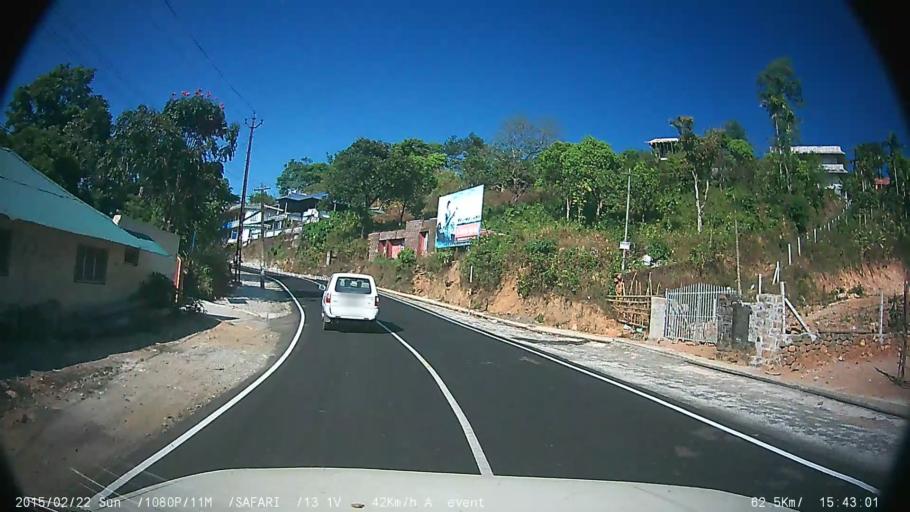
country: IN
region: Kerala
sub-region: Kottayam
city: Erattupetta
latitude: 9.5802
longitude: 76.9704
